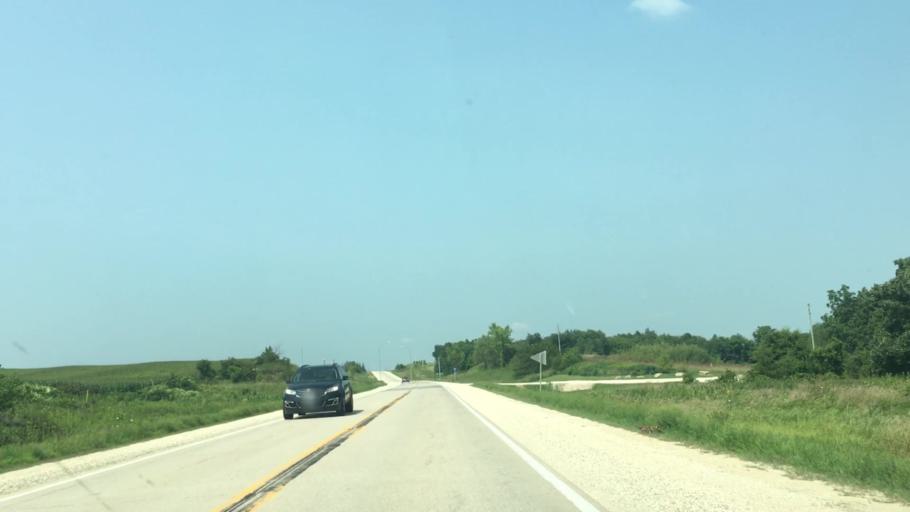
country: US
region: Iowa
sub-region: Fayette County
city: West Union
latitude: 43.1258
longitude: -91.8695
